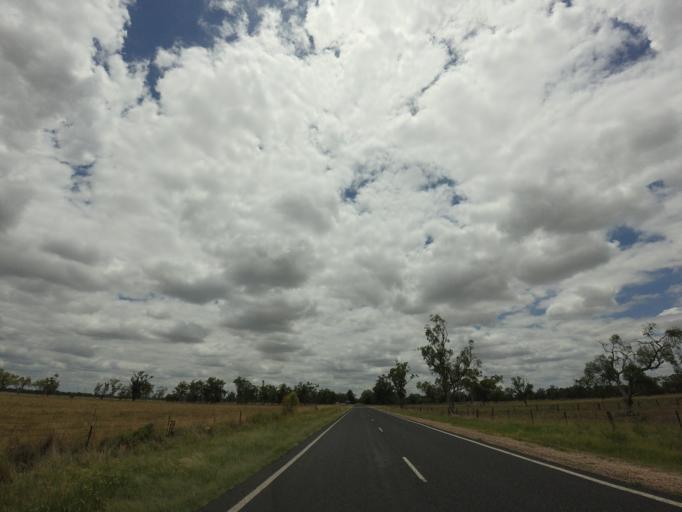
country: AU
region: Queensland
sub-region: Goondiwindi
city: Goondiwindi
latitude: -28.4997
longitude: 150.2917
